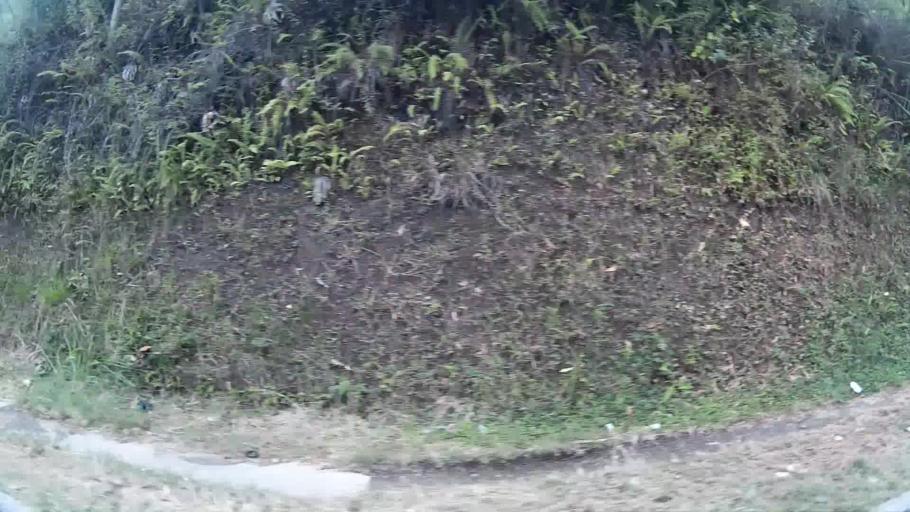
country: CO
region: Risaralda
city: Pereira
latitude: 4.8101
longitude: -75.7340
